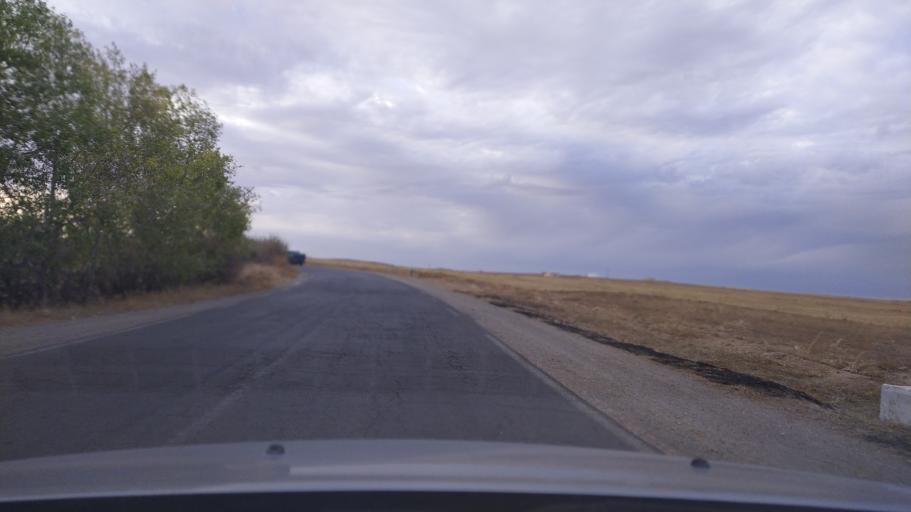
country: DZ
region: Tiaret
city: Frenda
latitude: 34.9845
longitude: 1.1416
